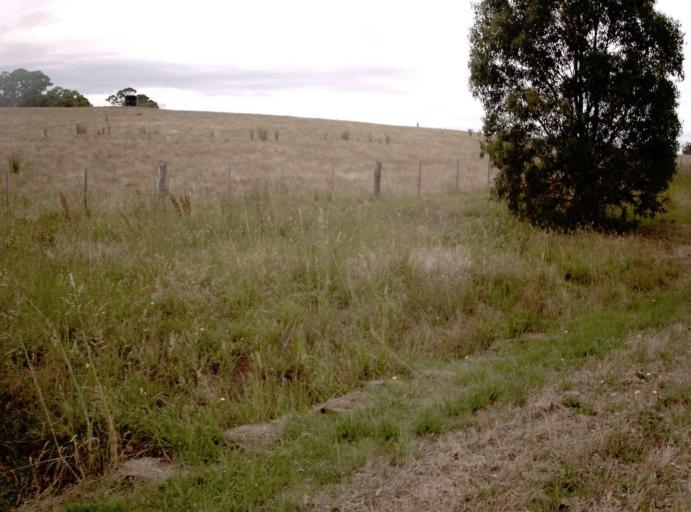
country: AU
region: Victoria
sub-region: East Gippsland
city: Bairnsdale
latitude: -37.7900
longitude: 147.3811
